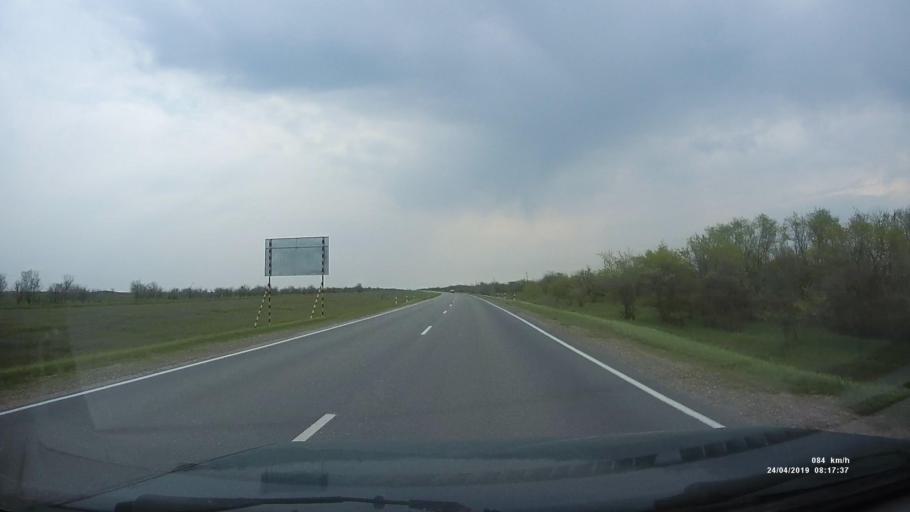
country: RU
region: Kalmykiya
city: Priyutnoye
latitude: 46.0970
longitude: 43.6344
